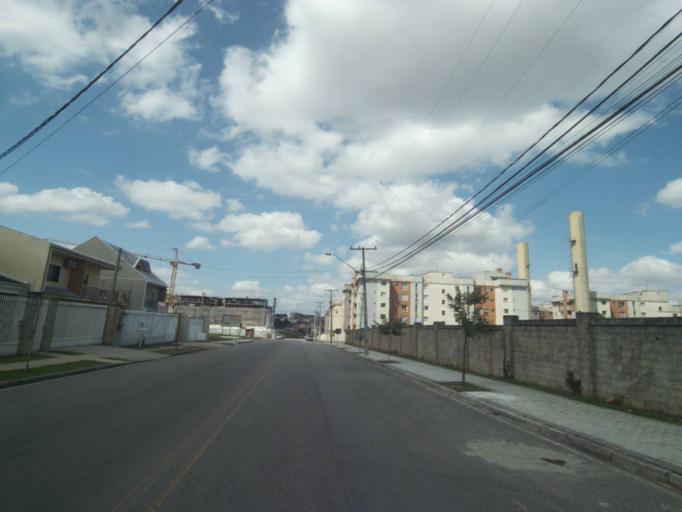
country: BR
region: Parana
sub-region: Curitiba
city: Curitiba
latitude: -25.5030
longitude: -49.3106
